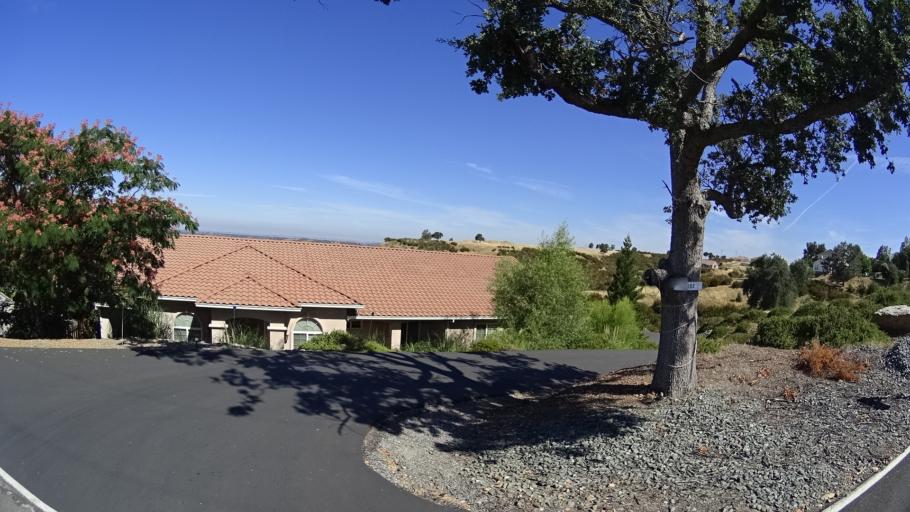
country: US
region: California
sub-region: Calaveras County
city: Rancho Calaveras
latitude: 38.1662
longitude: -120.8666
